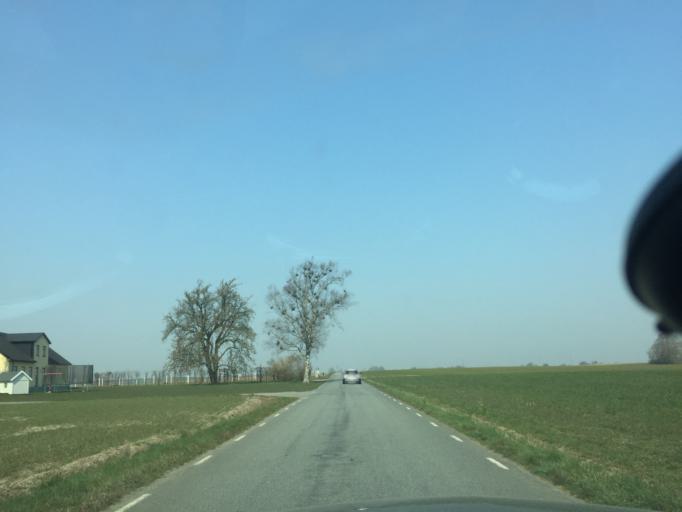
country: SE
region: Skane
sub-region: Simrishamns Kommun
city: Simrishamn
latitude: 55.4573
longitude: 14.2132
